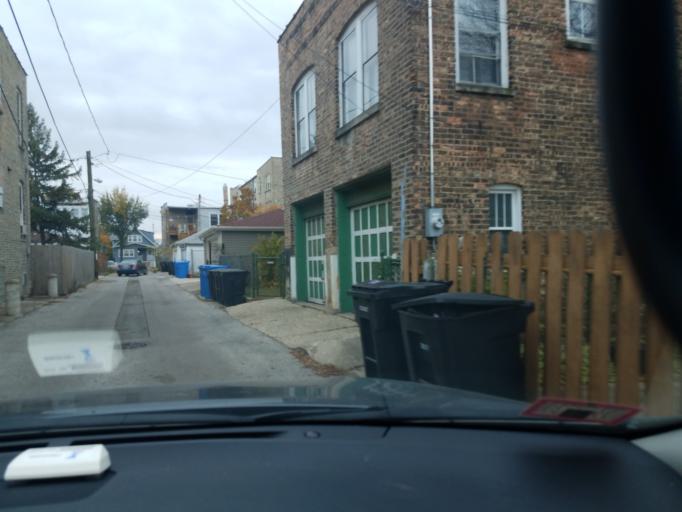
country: US
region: Illinois
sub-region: Cook County
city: Lincolnwood
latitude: 41.9472
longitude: -87.7299
